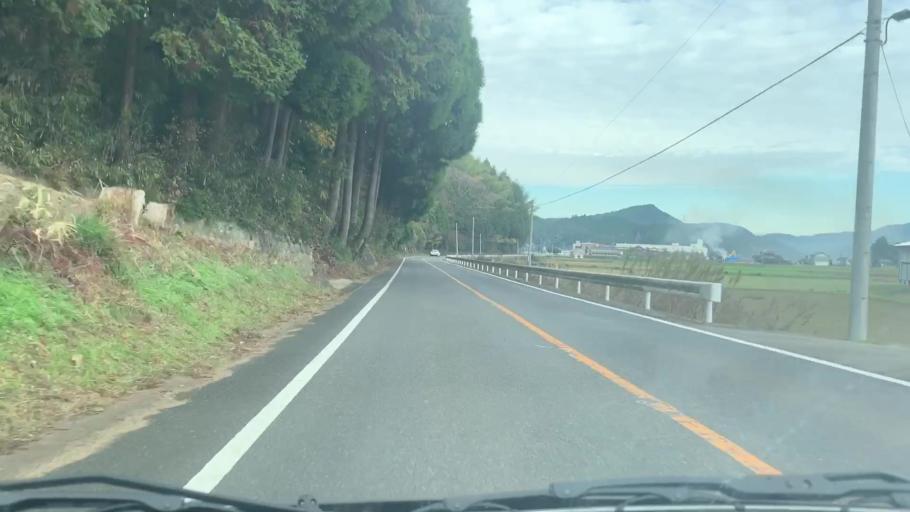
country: JP
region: Saga Prefecture
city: Takeocho-takeo
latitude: 33.2219
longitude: 129.9649
